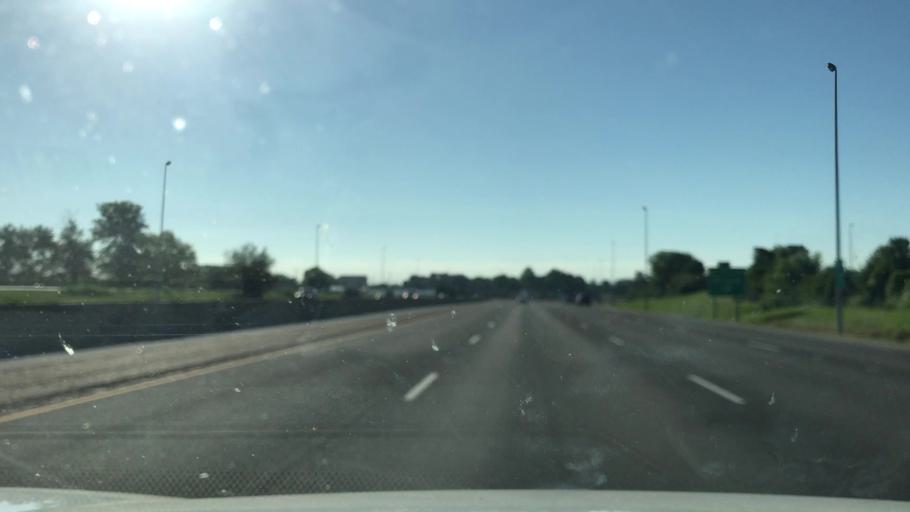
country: US
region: Illinois
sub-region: Saint Clair County
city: Fairview Heights
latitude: 38.5965
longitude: -89.9540
